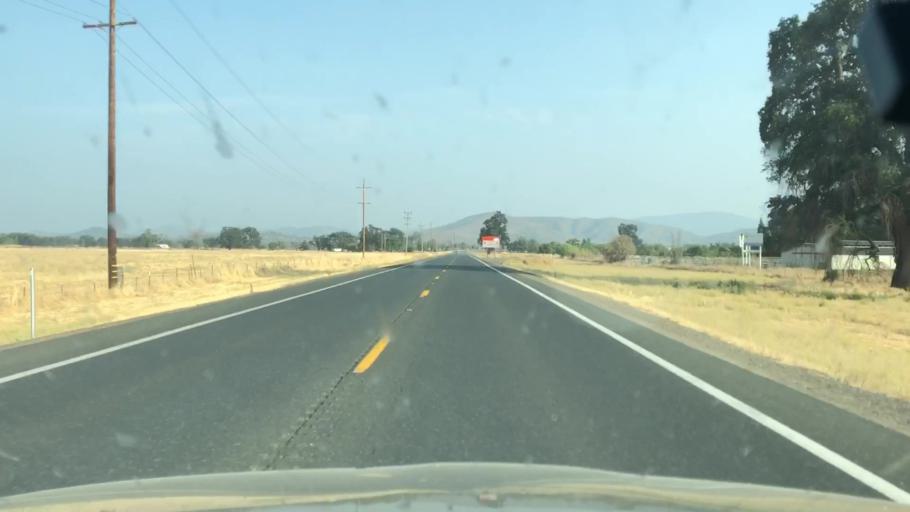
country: US
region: California
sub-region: Lake County
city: Hidden Valley Lake
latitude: 38.8002
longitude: -122.5710
